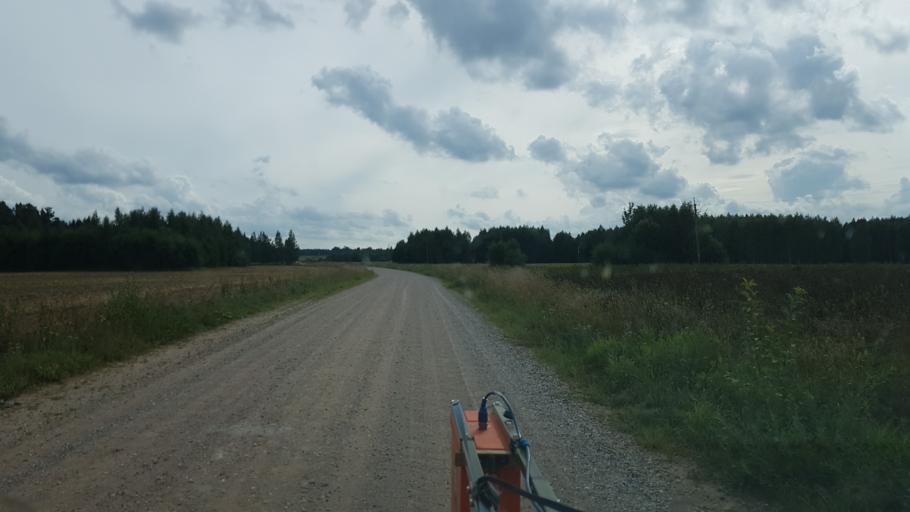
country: RU
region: Pskov
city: Pechory
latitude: 57.8127
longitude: 27.5130
